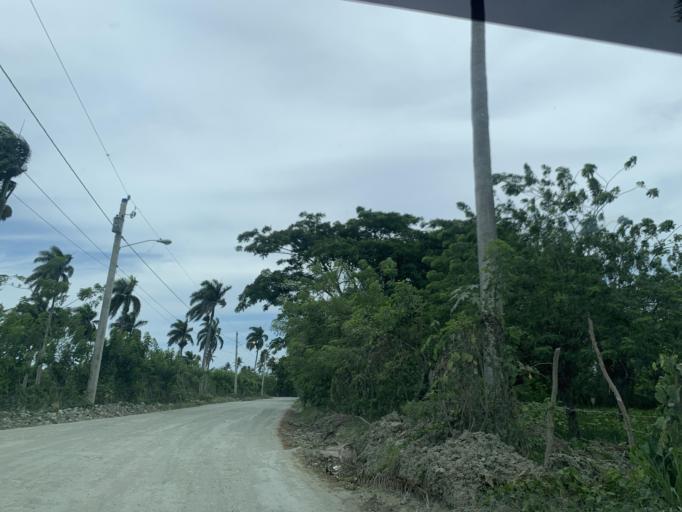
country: DO
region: Puerto Plata
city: Imbert
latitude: 19.8264
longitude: -70.7861
